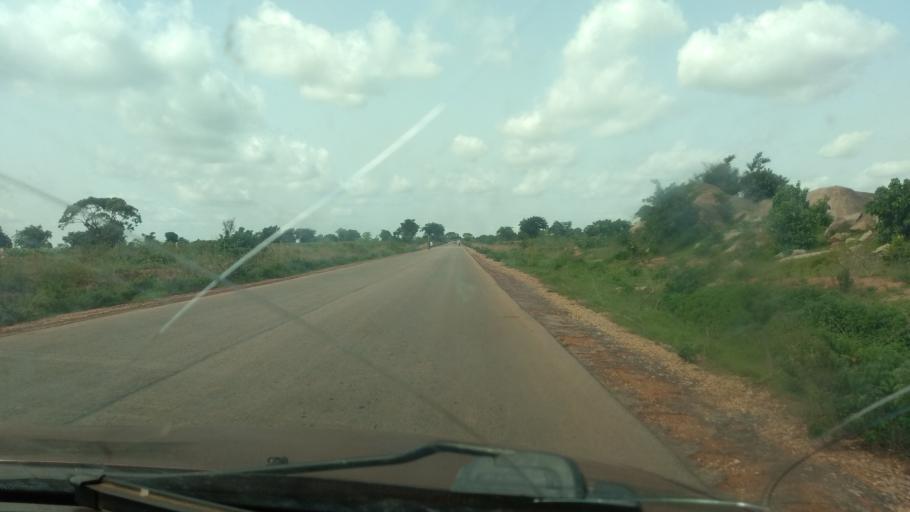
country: NG
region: Katsina
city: Sabuwa
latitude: 11.0507
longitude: 7.1597
